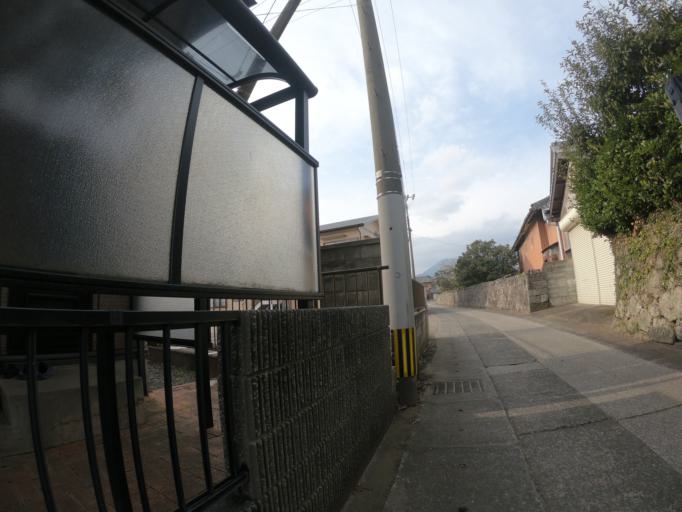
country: JP
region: Nagasaki
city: Shimabara
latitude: 32.6691
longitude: 130.3065
